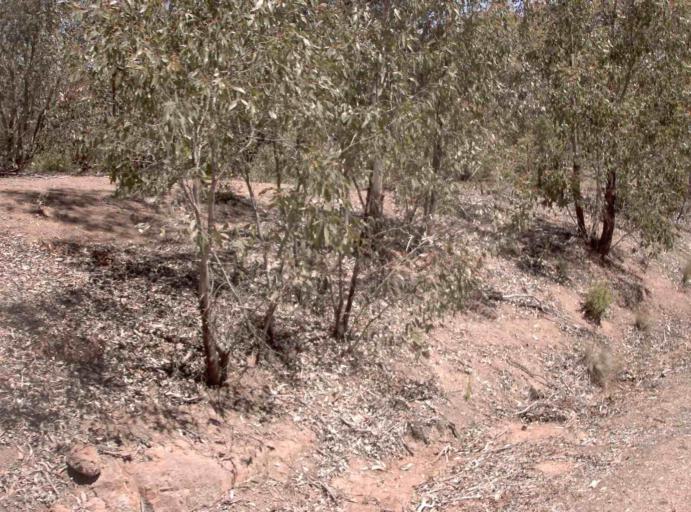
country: AU
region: New South Wales
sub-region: Snowy River
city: Jindabyne
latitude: -37.0762
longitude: 148.2603
